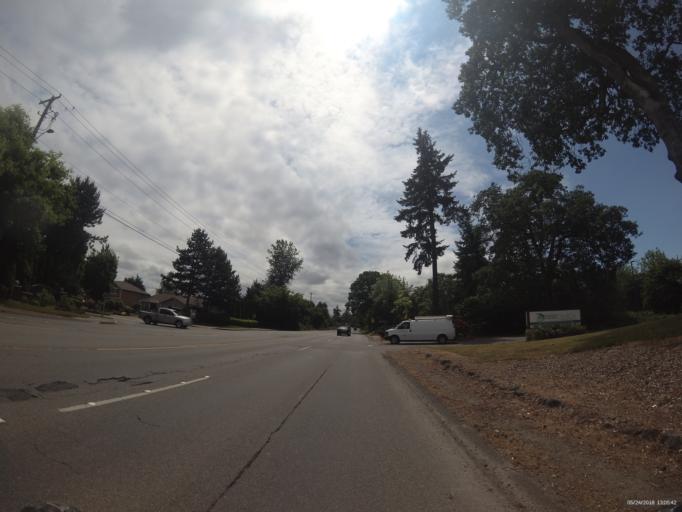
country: US
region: Washington
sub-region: Pierce County
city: Lakewood
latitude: 47.1845
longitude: -122.5087
